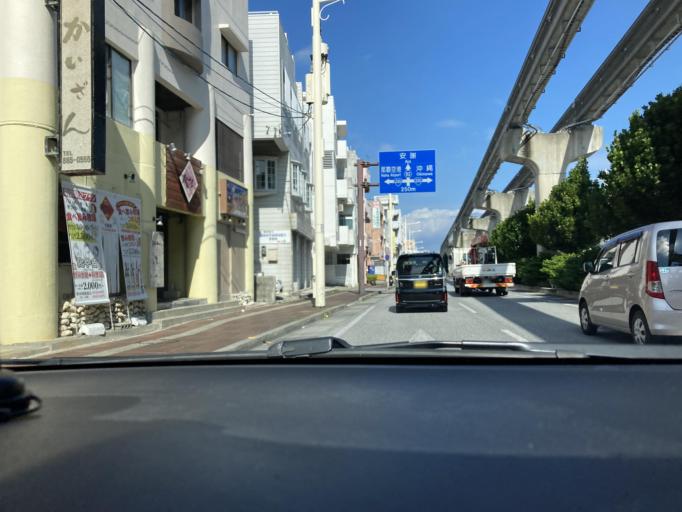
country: JP
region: Okinawa
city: Naha-shi
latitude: 26.2296
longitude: 127.7070
